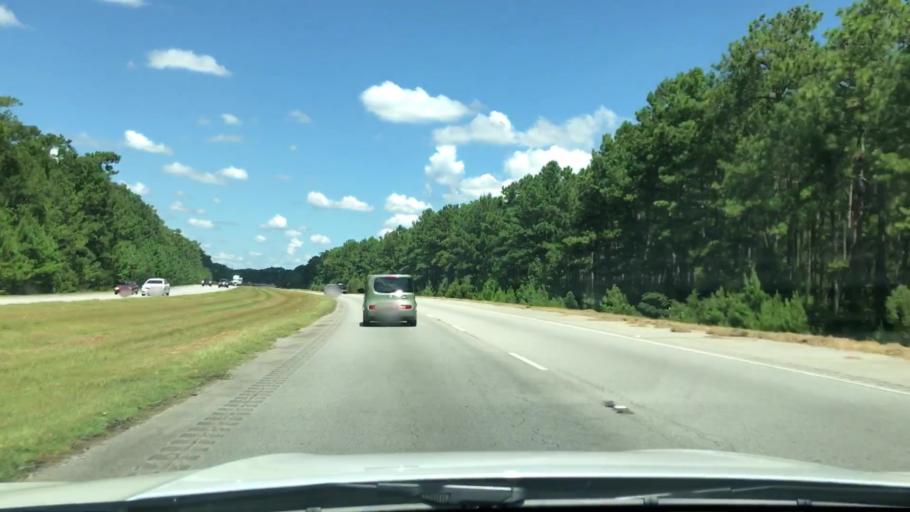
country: US
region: South Carolina
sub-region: Berkeley County
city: Hanahan
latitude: 32.9510
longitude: -80.0000
